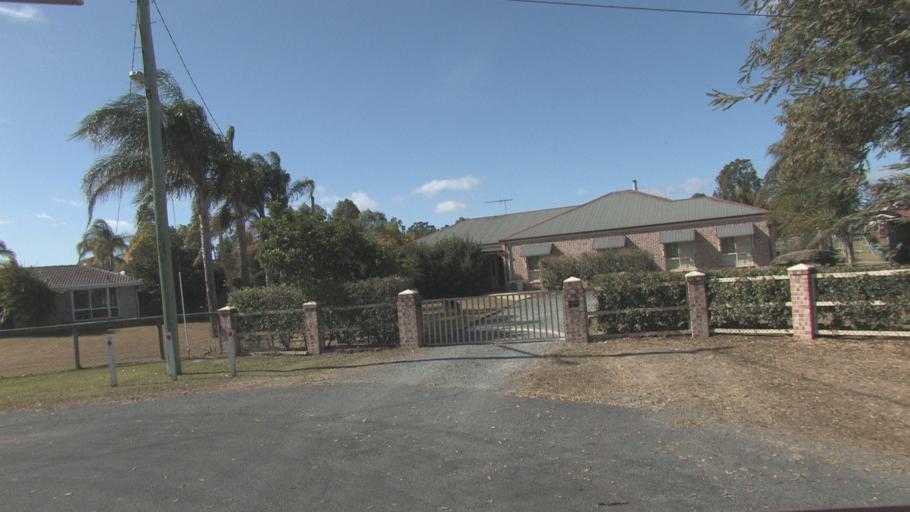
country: AU
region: Queensland
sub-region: Logan
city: Cedar Vale
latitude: -27.8640
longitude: 152.9671
